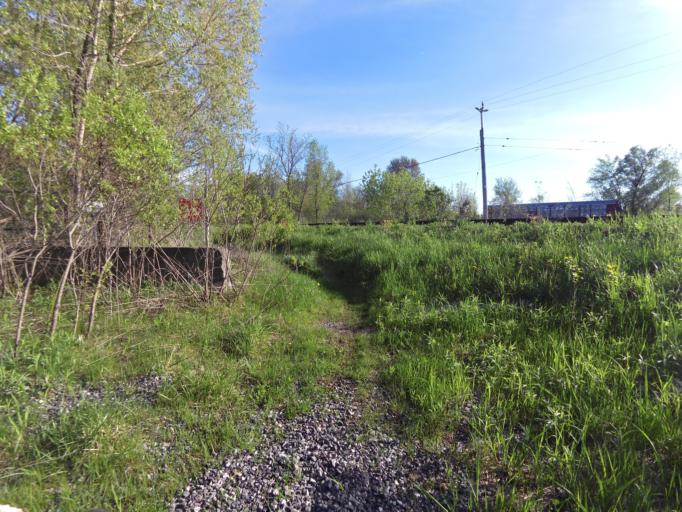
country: CA
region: Ontario
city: Ottawa
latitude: 45.3337
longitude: -75.6437
